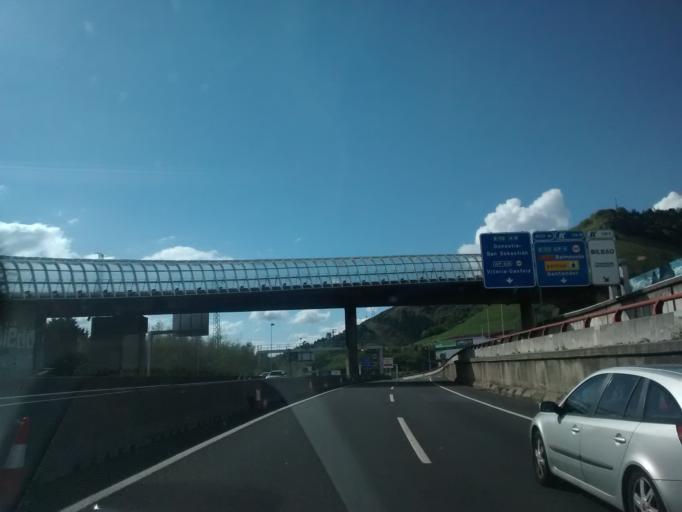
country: ES
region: Basque Country
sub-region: Bizkaia
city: Bilbao
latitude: 43.2522
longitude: -2.9464
